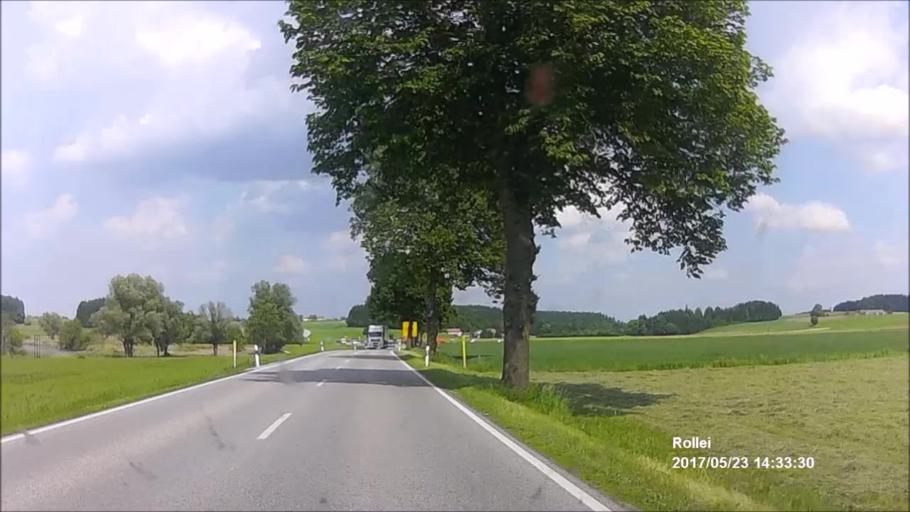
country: DE
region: Bavaria
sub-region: Upper Bavaria
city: Obing
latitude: 48.0001
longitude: 12.4170
